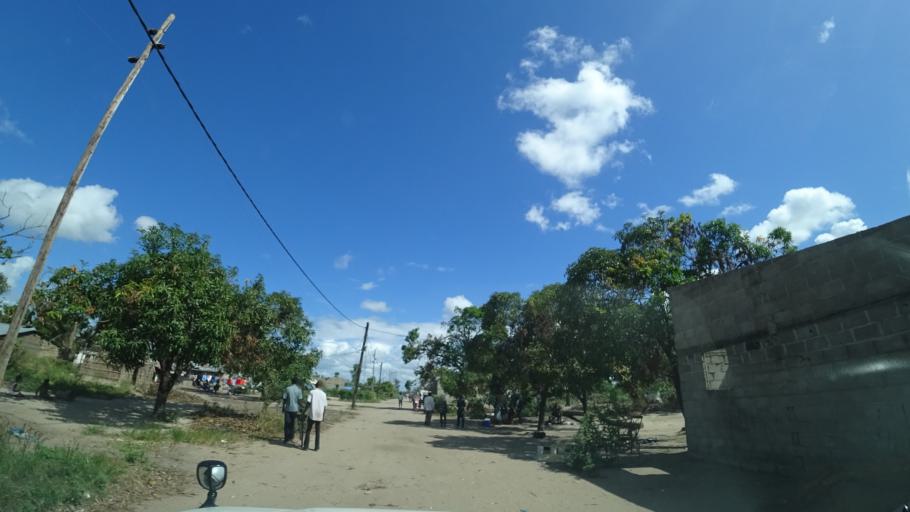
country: MZ
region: Sofala
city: Dondo
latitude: -19.4983
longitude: 34.5980
